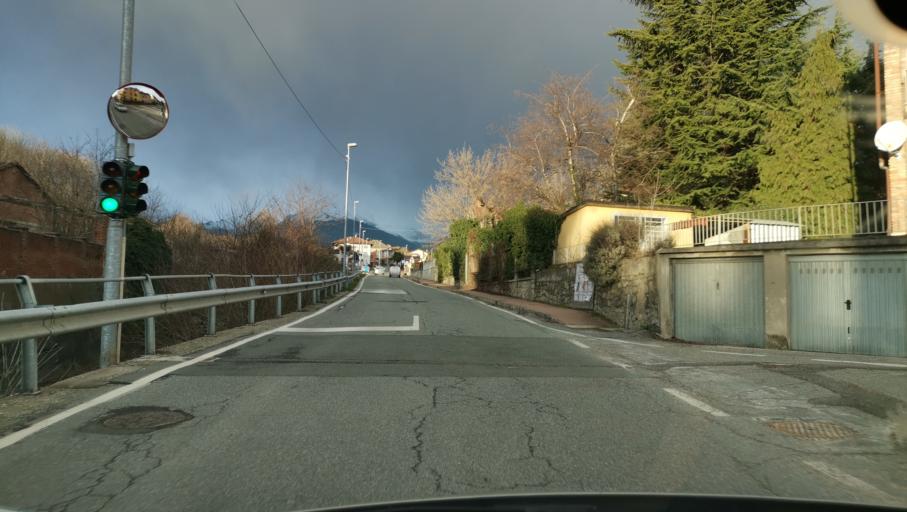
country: IT
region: Piedmont
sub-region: Provincia di Torino
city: Giaveno
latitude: 45.0455
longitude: 7.3492
